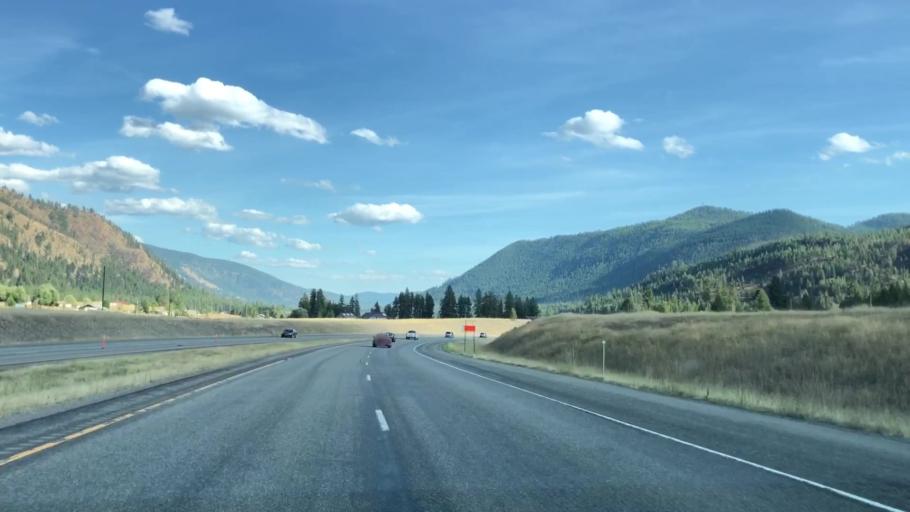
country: US
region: Montana
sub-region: Mineral County
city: Superior
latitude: 47.2122
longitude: -114.9396
